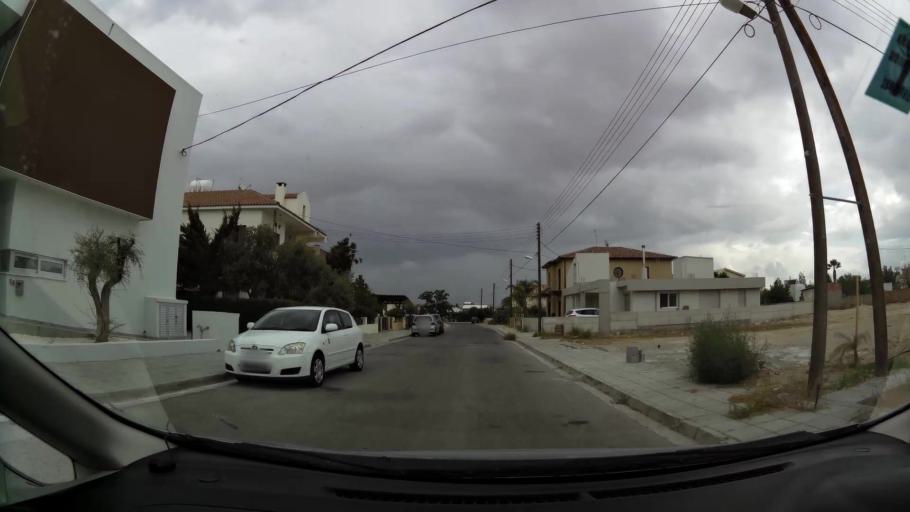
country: CY
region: Lefkosia
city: Geri
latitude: 35.1118
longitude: 33.3904
